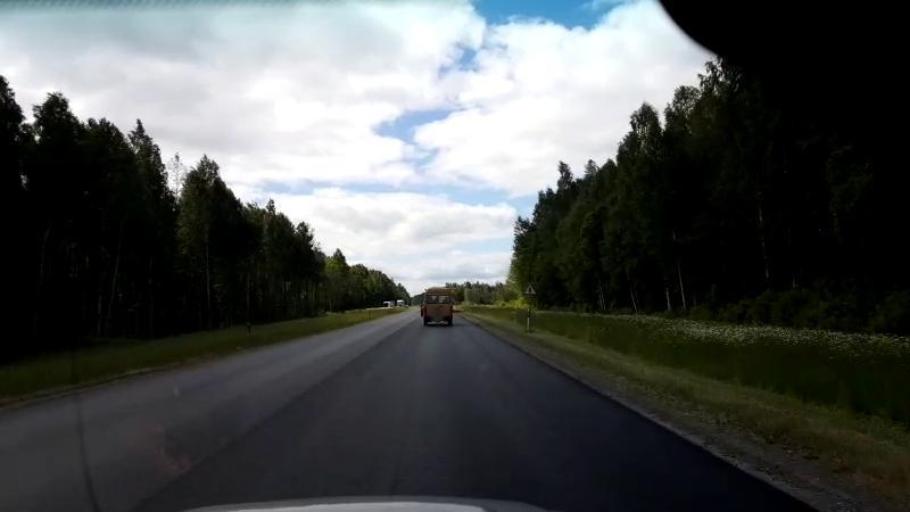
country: LV
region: Salacgrivas
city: Ainazi
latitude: 57.9684
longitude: 24.4490
